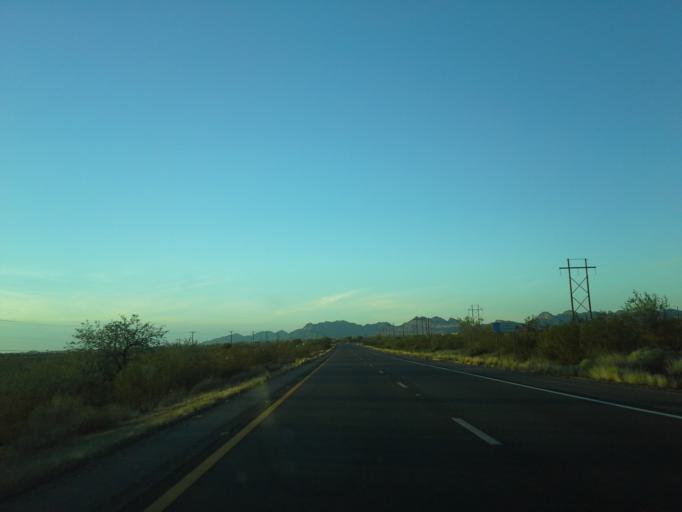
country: US
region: Arizona
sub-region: Pinal County
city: Apache Junction
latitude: 33.3763
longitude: -111.4872
